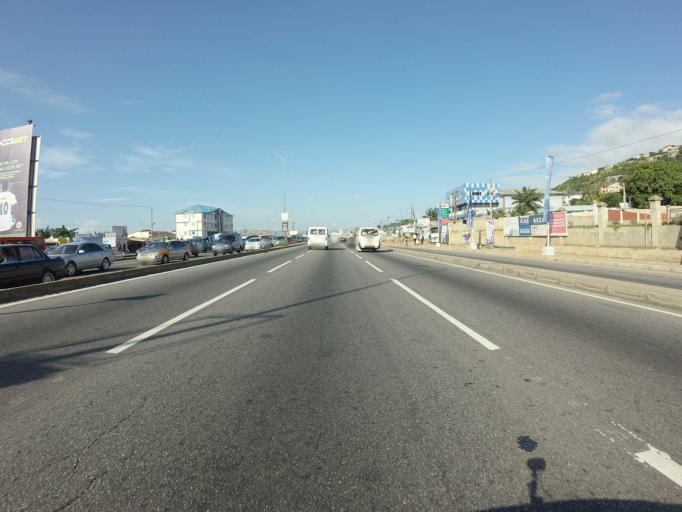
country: GH
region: Greater Accra
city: Gbawe
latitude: 5.5585
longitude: -0.2965
